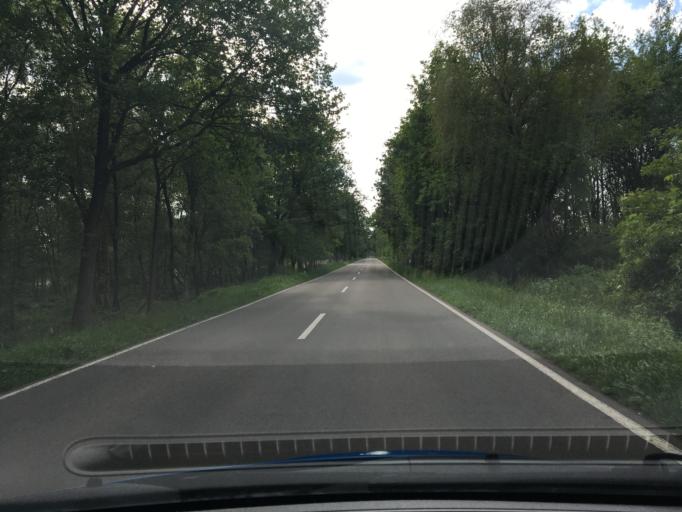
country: DE
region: Lower Saxony
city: Wistedt
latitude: 53.2724
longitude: 9.6531
